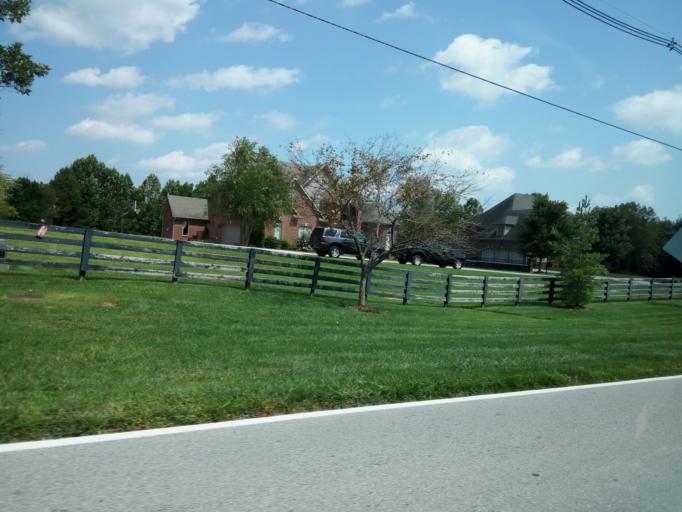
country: US
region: Kentucky
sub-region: Oldham County
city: Pewee Valley
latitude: 38.2848
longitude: -85.4898
